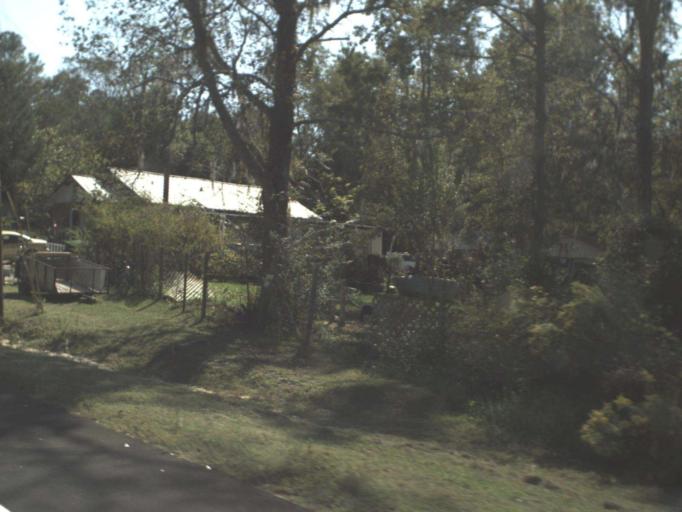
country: US
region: Alabama
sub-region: Covington County
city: Florala
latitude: 30.9869
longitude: -86.3094
